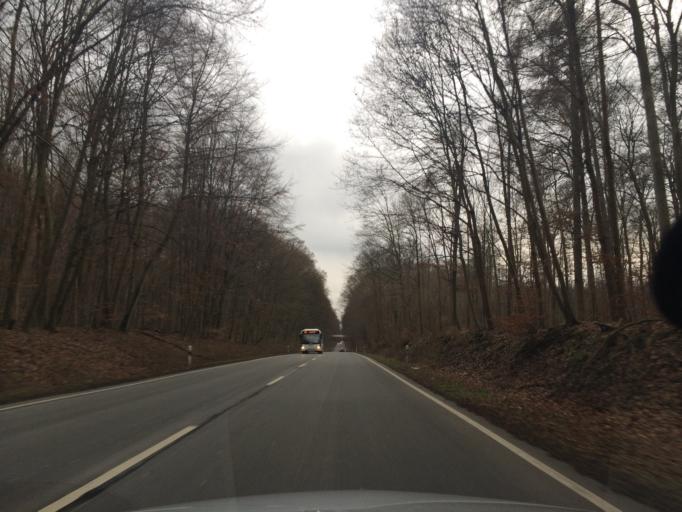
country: DE
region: Hesse
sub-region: Regierungsbezirk Darmstadt
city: Neu Isenburg
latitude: 50.0791
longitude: 8.6924
